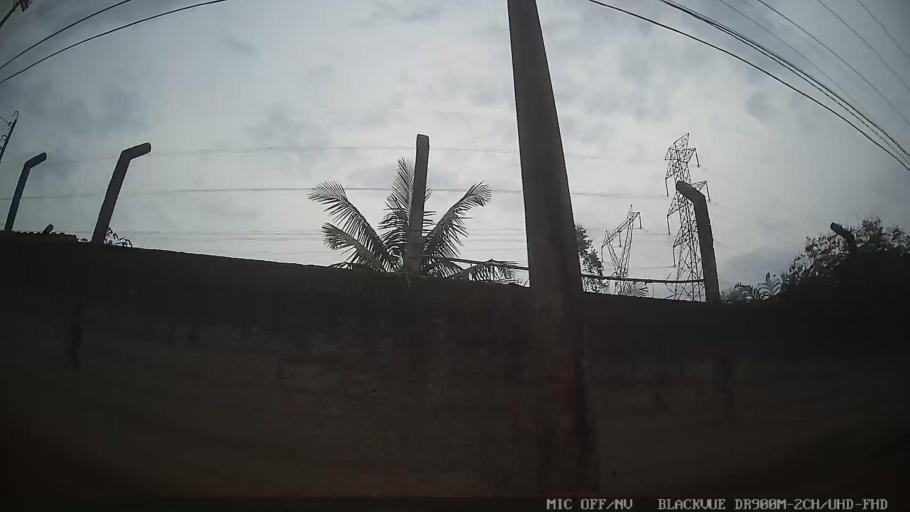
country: BR
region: Sao Paulo
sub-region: Suzano
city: Suzano
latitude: -23.6544
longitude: -46.2841
